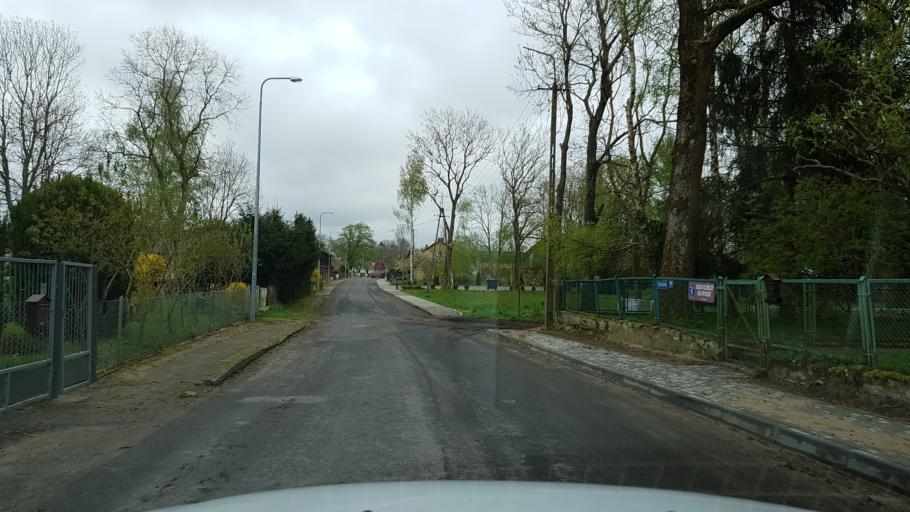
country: PL
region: West Pomeranian Voivodeship
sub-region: Powiat kolobrzeski
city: Ryman
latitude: 54.0305
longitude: 15.5264
